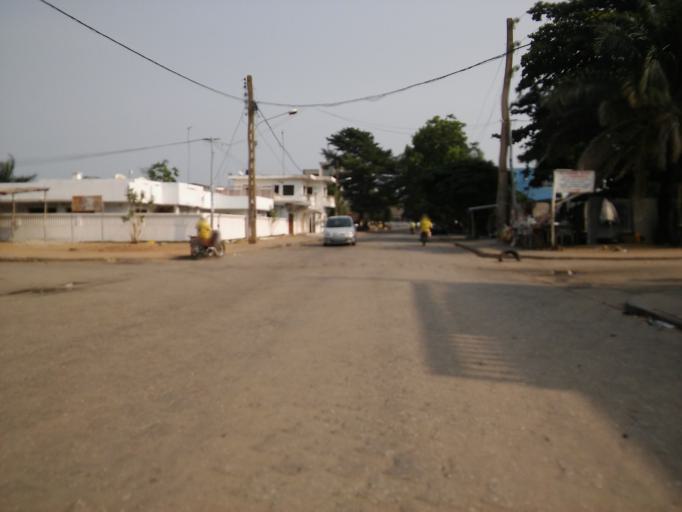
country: BJ
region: Littoral
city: Cotonou
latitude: 6.3634
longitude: 2.4429
